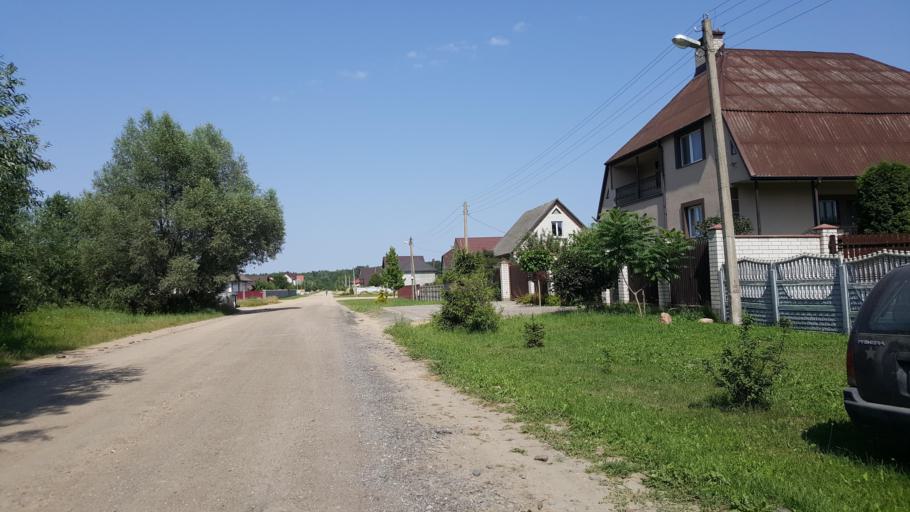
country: BY
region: Brest
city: Zhabinka
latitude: 52.1947
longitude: 24.0389
